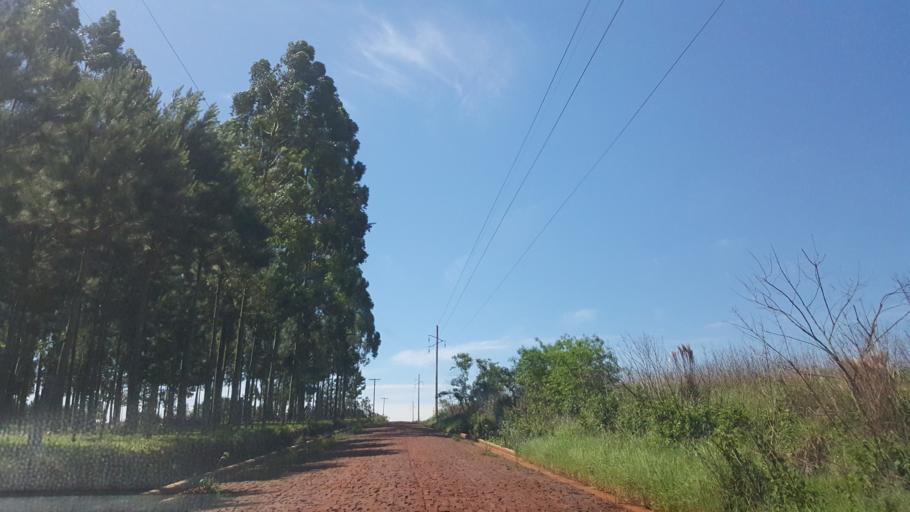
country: AR
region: Misiones
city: Capiovi
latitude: -26.9275
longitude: -55.0719
